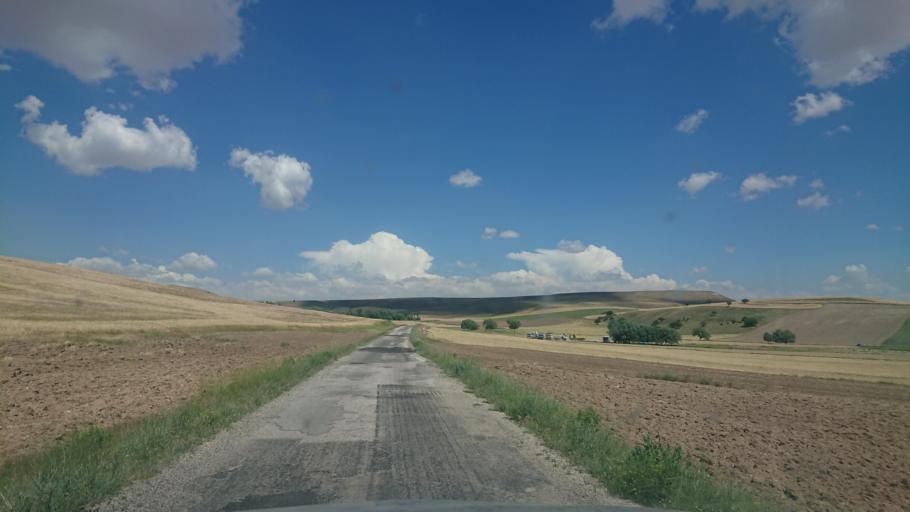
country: TR
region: Aksaray
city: Agacoren
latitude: 38.8000
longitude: 33.8209
